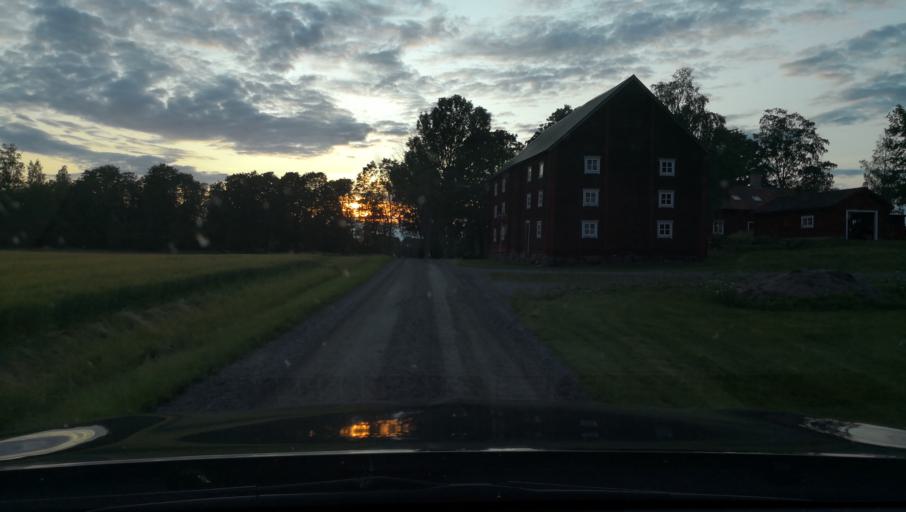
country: SE
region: Uppsala
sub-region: Osthammars Kommun
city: Bjorklinge
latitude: 60.0554
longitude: 17.6240
